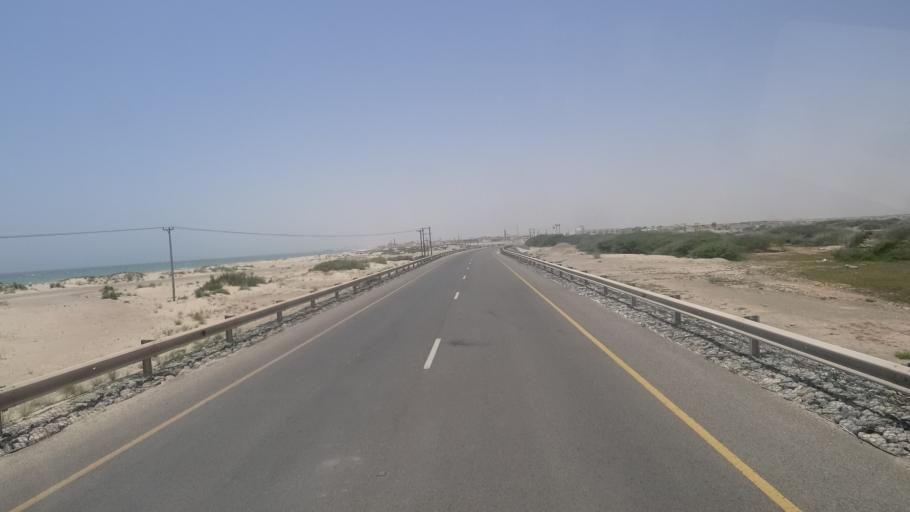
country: OM
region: Ash Sharqiyah
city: Sur
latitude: 22.0923
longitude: 59.6933
